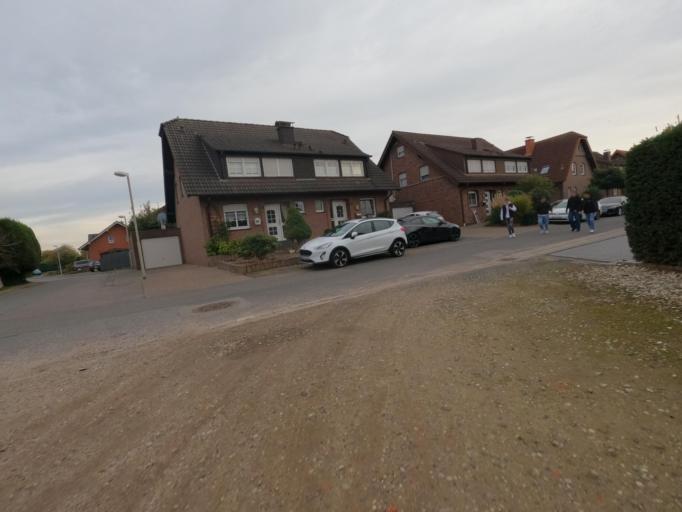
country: DE
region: North Rhine-Westphalia
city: Huckelhoven
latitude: 51.0456
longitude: 6.2231
